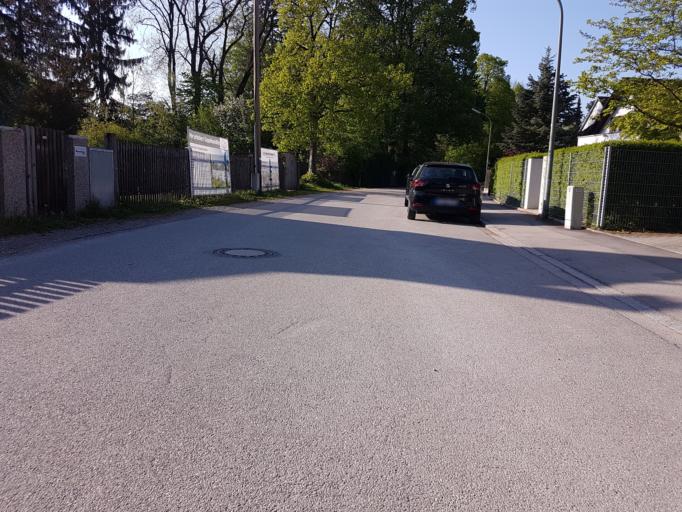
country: DE
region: Bavaria
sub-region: Upper Bavaria
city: Karlsfeld
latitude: 48.1930
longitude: 11.4581
